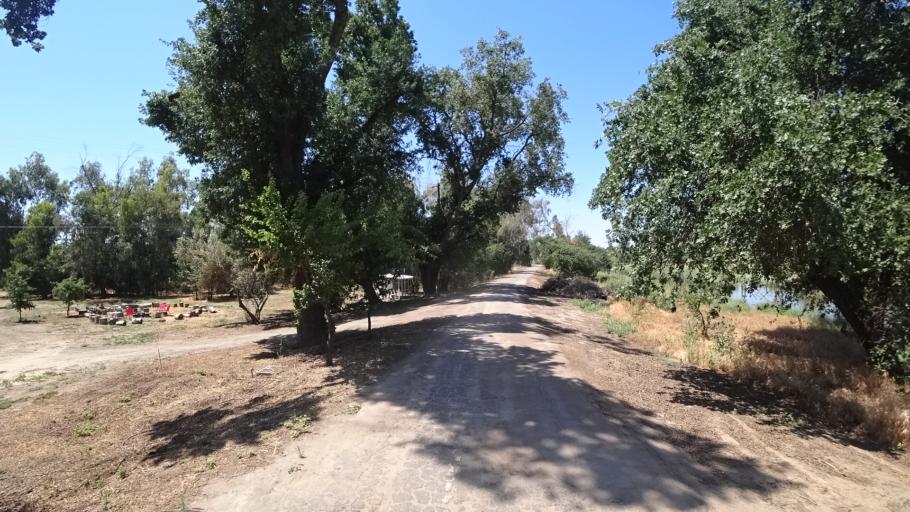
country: US
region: California
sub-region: Kings County
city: Lemoore
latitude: 36.3659
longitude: -119.8032
